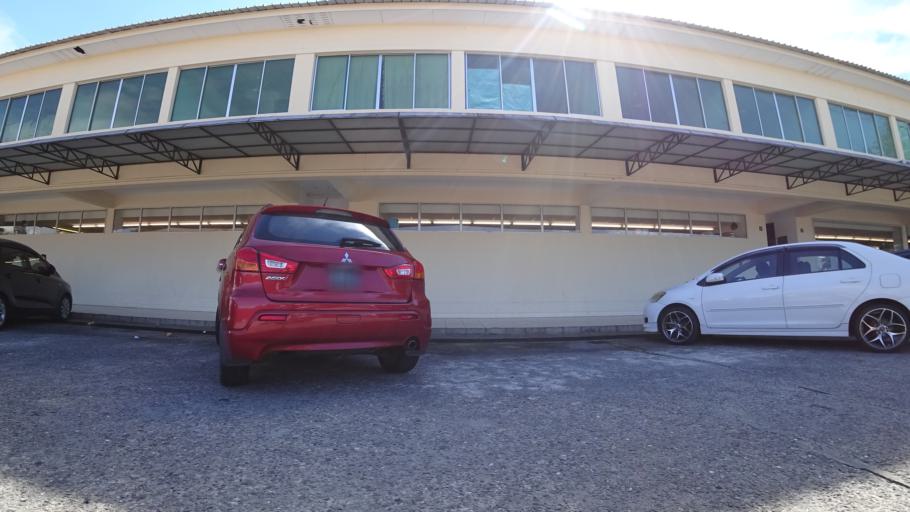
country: BN
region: Brunei and Muara
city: Bandar Seri Begawan
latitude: 4.8394
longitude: 114.8718
